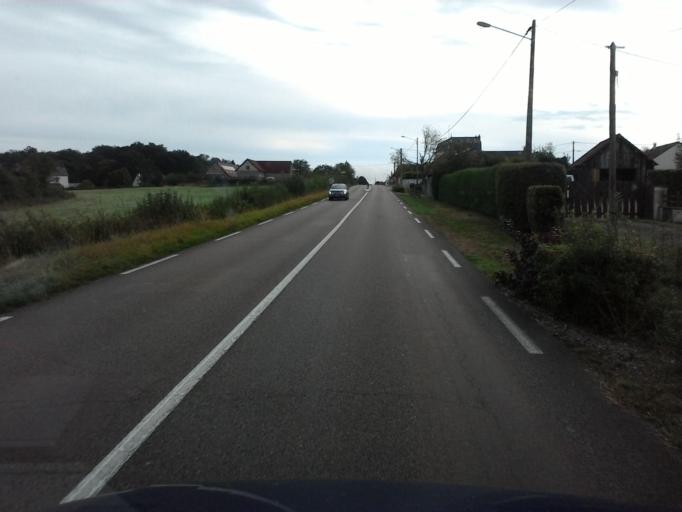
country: FR
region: Bourgogne
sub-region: Departement de Saone-et-Loire
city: Autun
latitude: 46.9969
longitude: 4.2325
